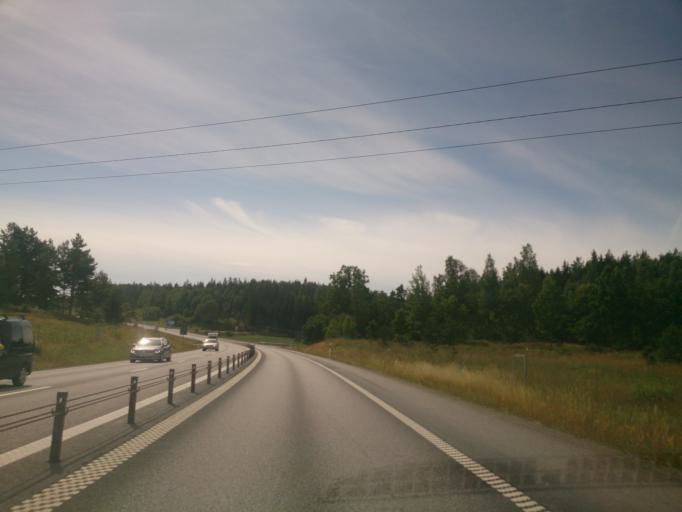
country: SE
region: OEstergoetland
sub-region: Valdemarsviks Kommun
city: Gusum
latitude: 58.2922
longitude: 16.4957
